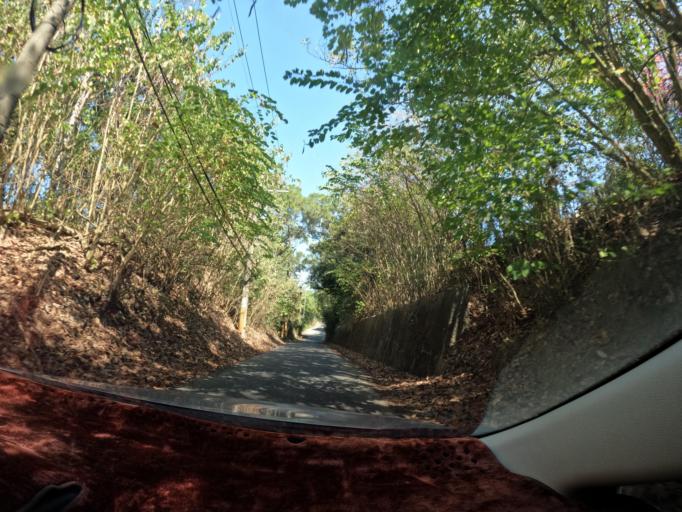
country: TW
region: Taiwan
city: Yujing
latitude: 23.0461
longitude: 120.3664
